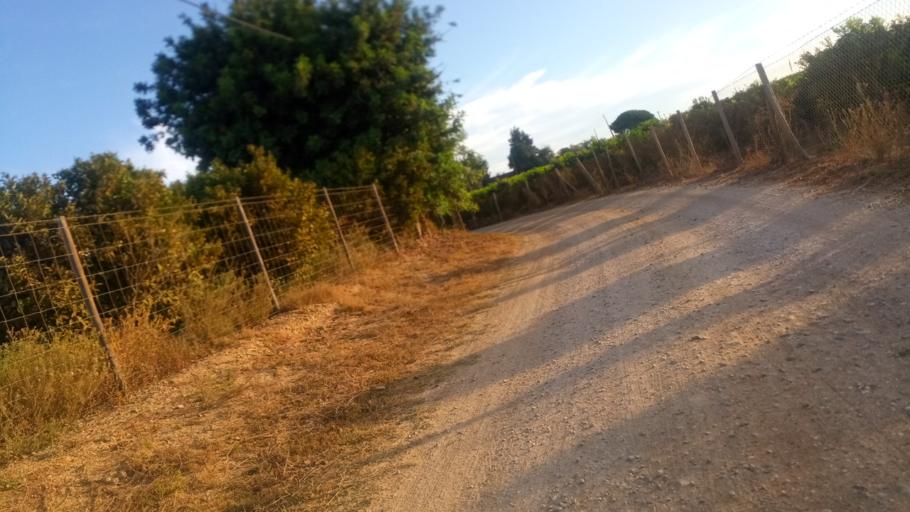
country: PT
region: Faro
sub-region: Tavira
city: Tavira
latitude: 37.1516
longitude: -7.5868
